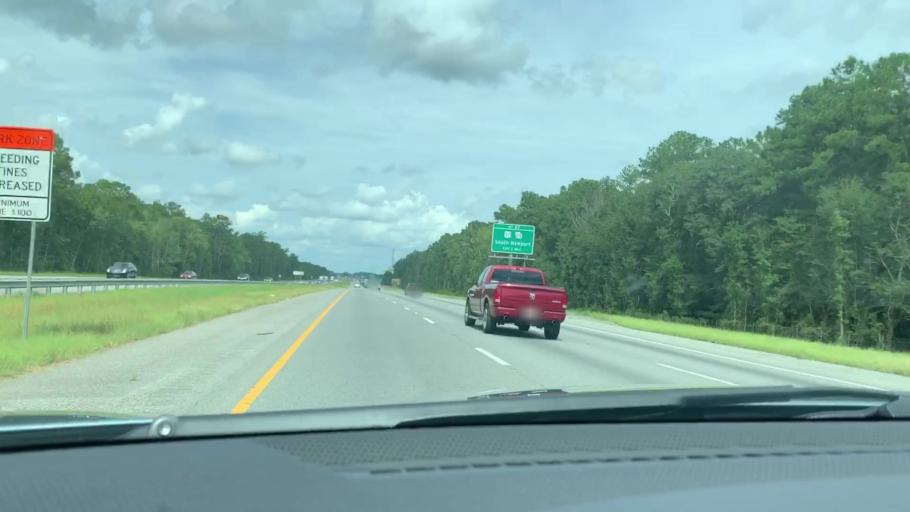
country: US
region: Georgia
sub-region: Liberty County
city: Midway
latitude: 31.6374
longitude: -81.4030
